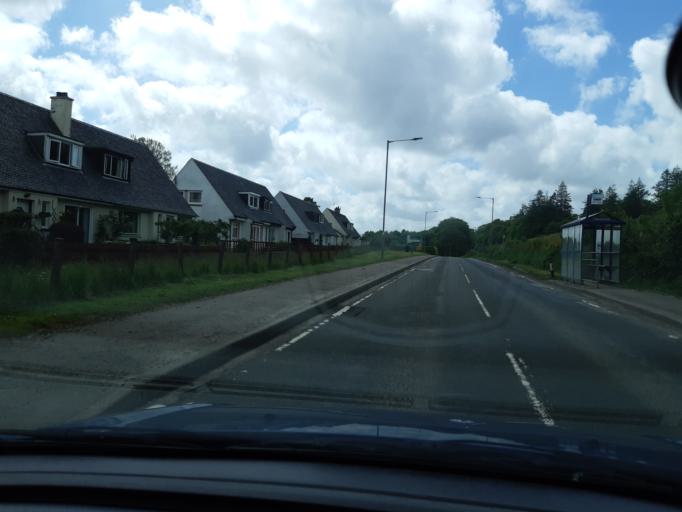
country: GB
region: Scotland
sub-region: Argyll and Bute
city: Lochgilphead
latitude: 56.0397
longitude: -5.4404
